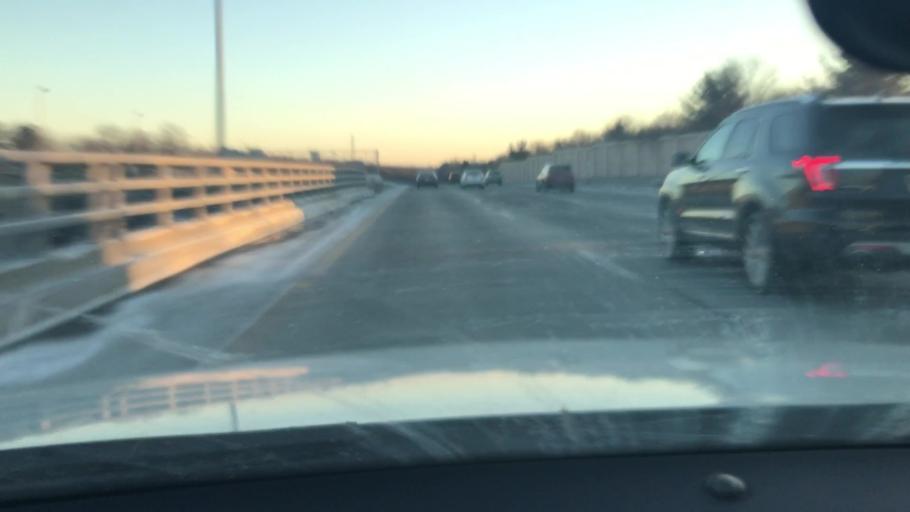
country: US
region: New Jersey
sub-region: Mercer County
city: Mercerville
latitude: 40.2327
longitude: -74.7005
